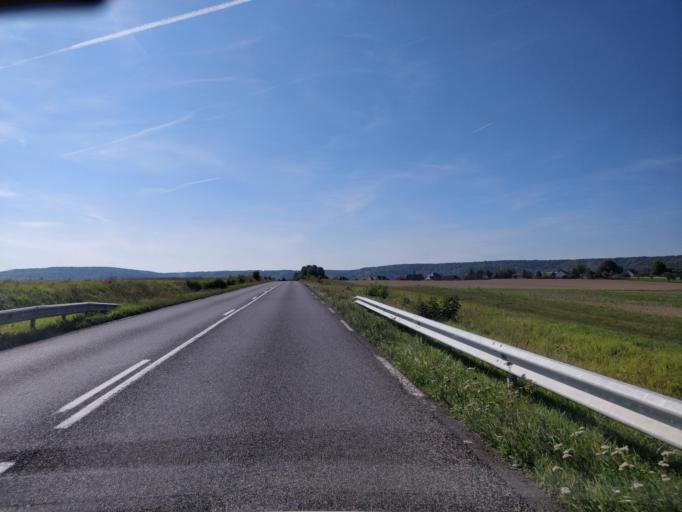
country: FR
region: Champagne-Ardenne
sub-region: Departement de l'Aube
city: Bouilly
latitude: 48.2064
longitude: 4.0054
